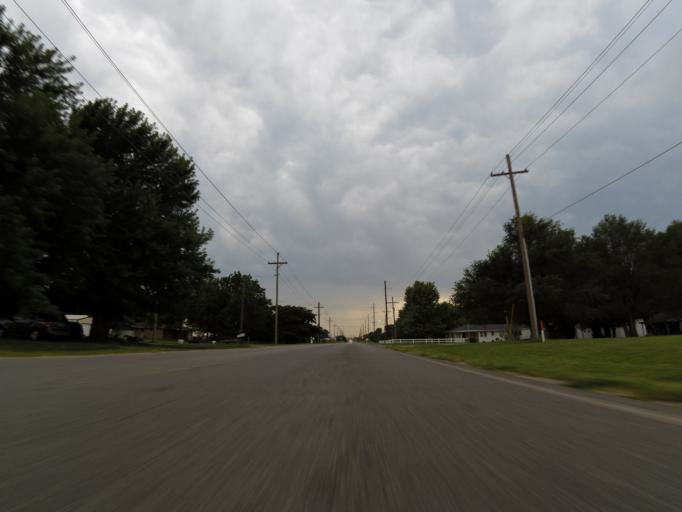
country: US
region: Kansas
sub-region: Reno County
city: South Hutchinson
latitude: 38.0280
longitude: -97.9664
